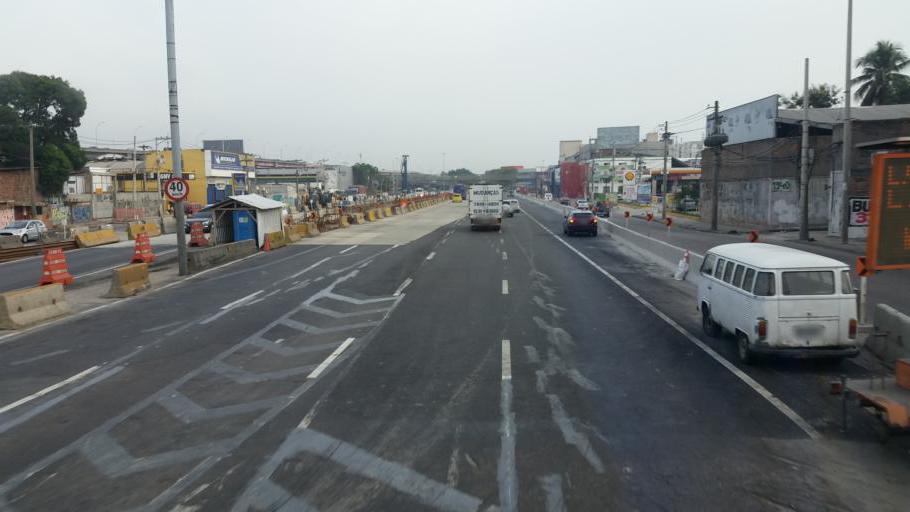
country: BR
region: Rio de Janeiro
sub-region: Rio De Janeiro
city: Rio de Janeiro
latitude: -22.8877
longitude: -43.2236
